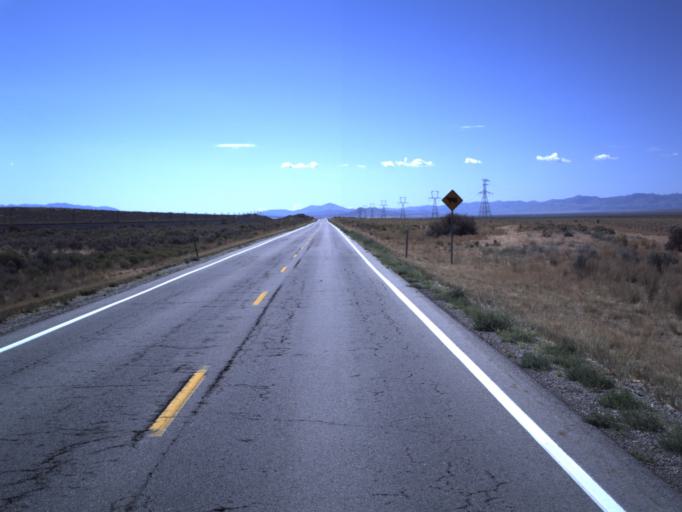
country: US
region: Utah
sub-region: Tooele County
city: Tooele
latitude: 40.3604
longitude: -112.4140
